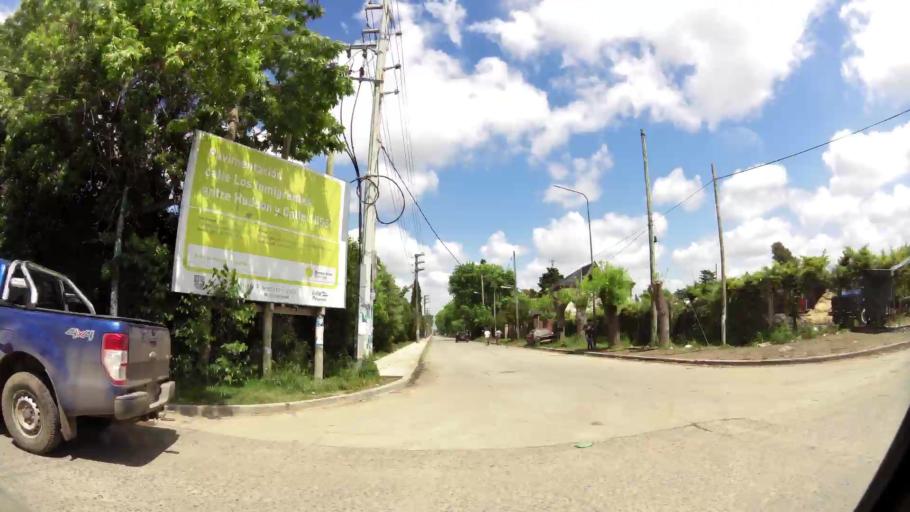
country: AR
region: Buenos Aires
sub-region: Partido de Quilmes
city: Quilmes
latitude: -34.8383
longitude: -58.2373
